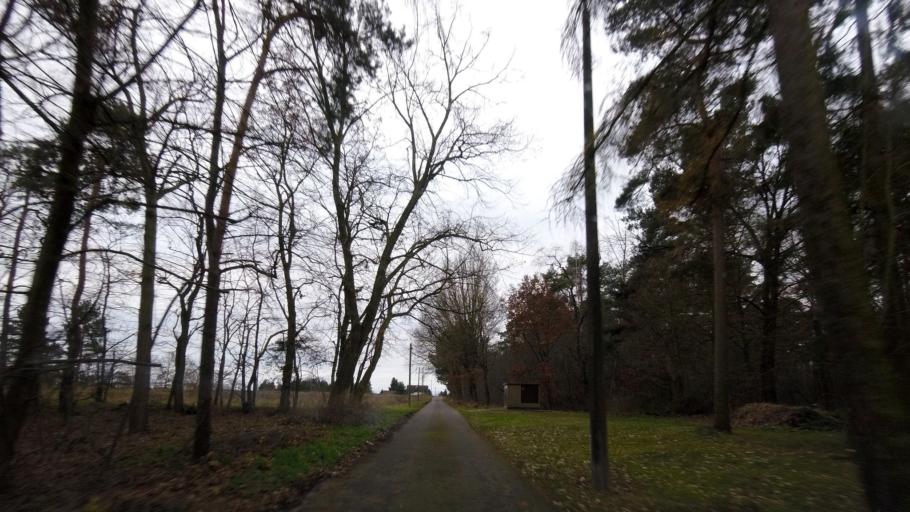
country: DE
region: Brandenburg
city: Niedergorsdorf
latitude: 51.9855
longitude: 12.9918
